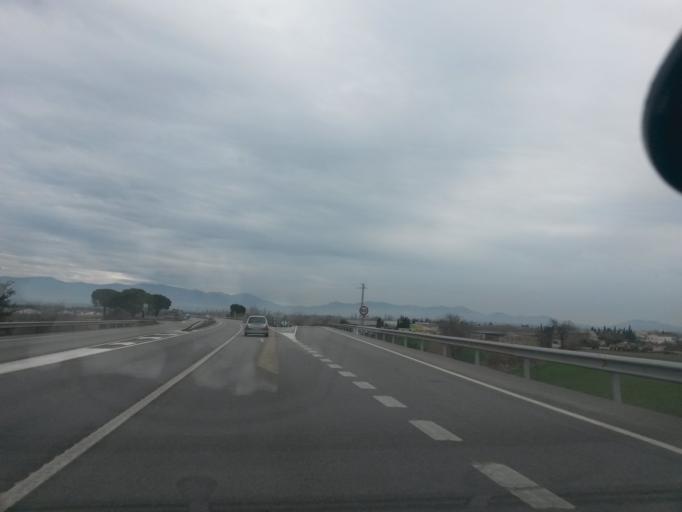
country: ES
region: Catalonia
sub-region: Provincia de Girona
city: Vilabertran
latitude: 42.2645
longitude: 2.9880
